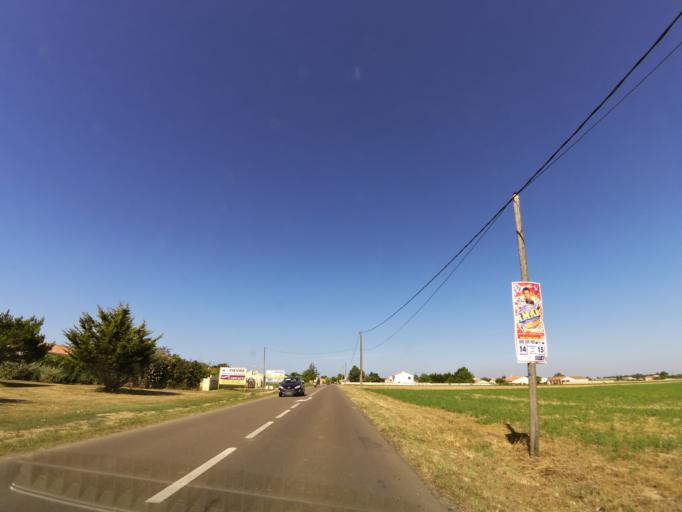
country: FR
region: Pays de la Loire
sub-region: Departement de la Vendee
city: Jard-sur-Mer
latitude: 46.4196
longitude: -1.5592
